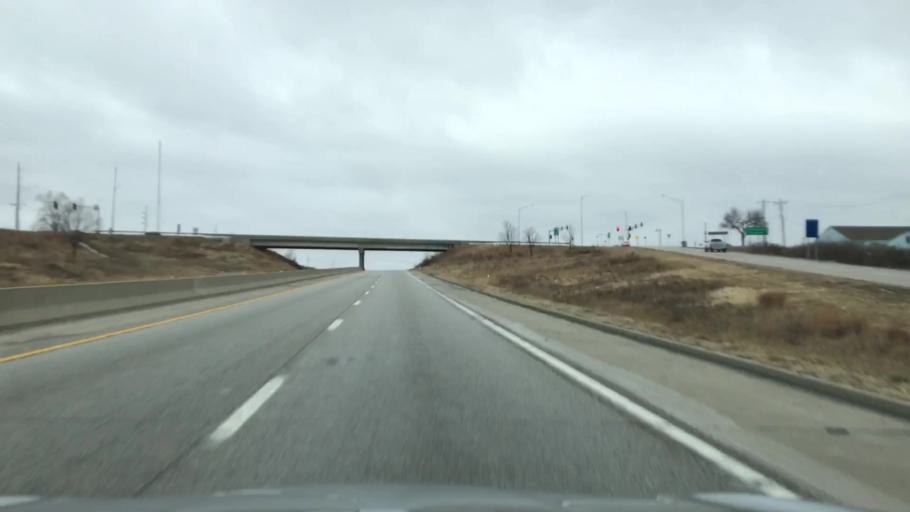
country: US
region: Missouri
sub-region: Jackson County
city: East Independence
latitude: 39.1152
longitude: -94.3841
